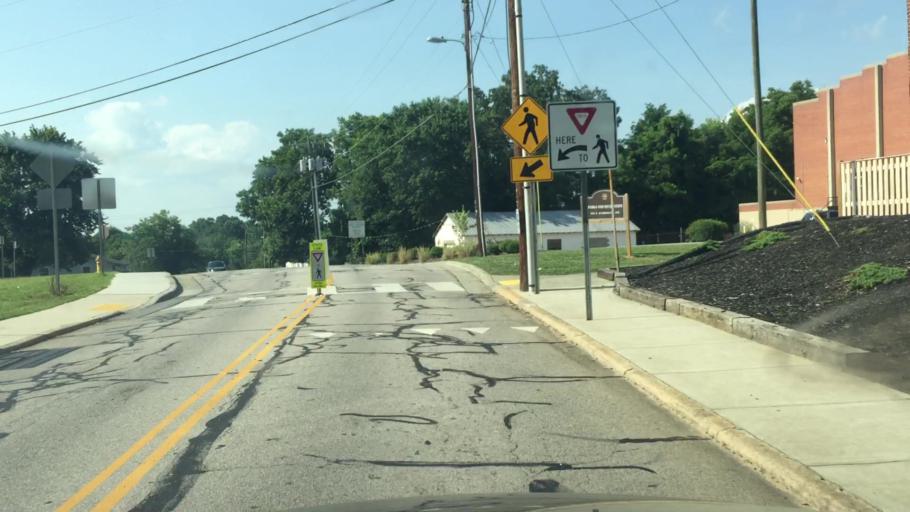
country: US
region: North Carolina
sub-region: Rockingham County
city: Reidsville
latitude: 36.3626
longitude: -79.6710
